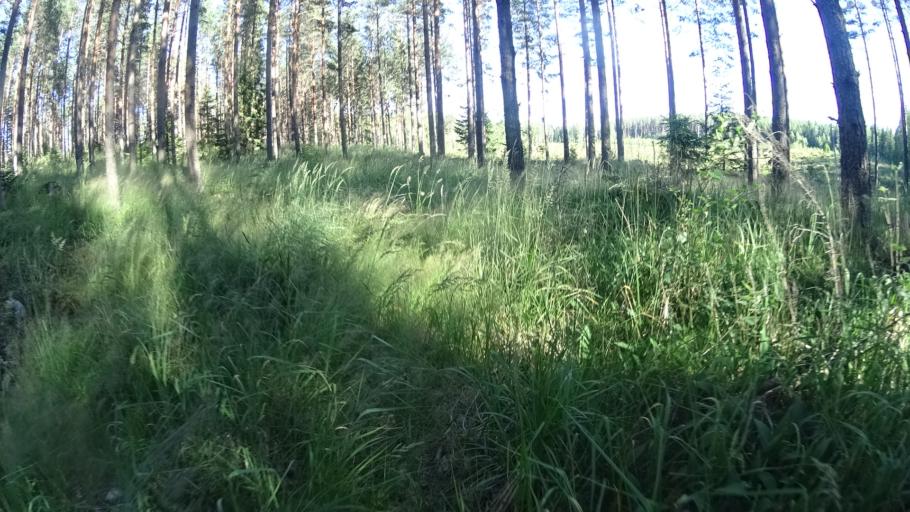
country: FI
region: Uusimaa
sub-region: Helsinki
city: Karkkila
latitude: 60.6508
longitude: 24.1545
